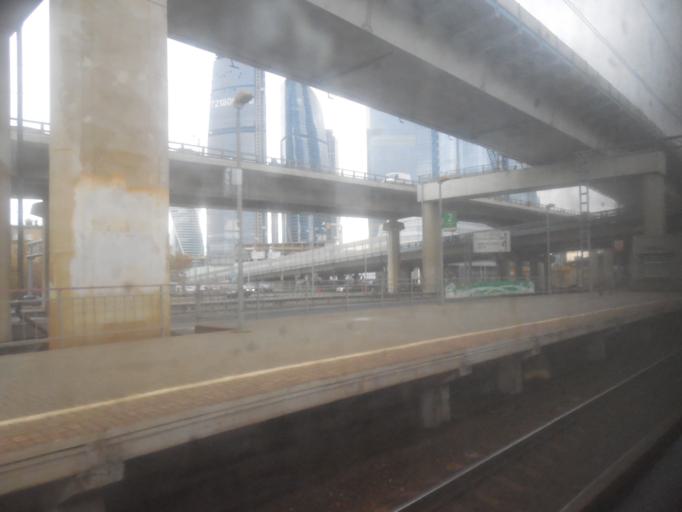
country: RU
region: Moskovskaya
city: Presnenskiy
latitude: 55.7540
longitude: 37.5317
